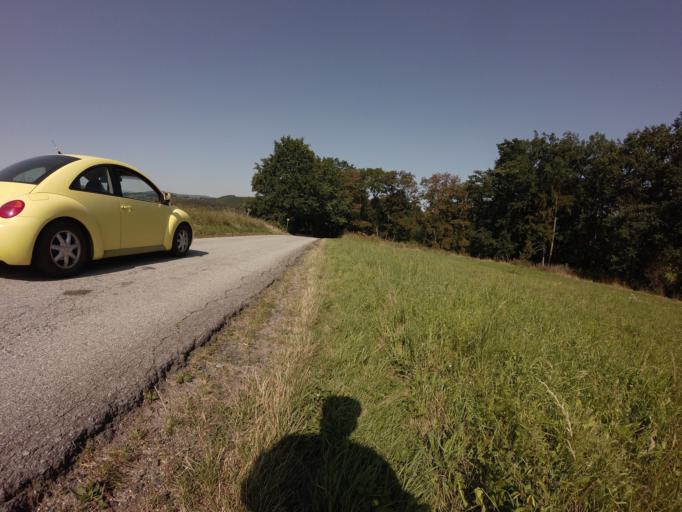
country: CZ
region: Jihocesky
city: Kamenny Ujezd
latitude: 48.9136
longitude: 14.4304
